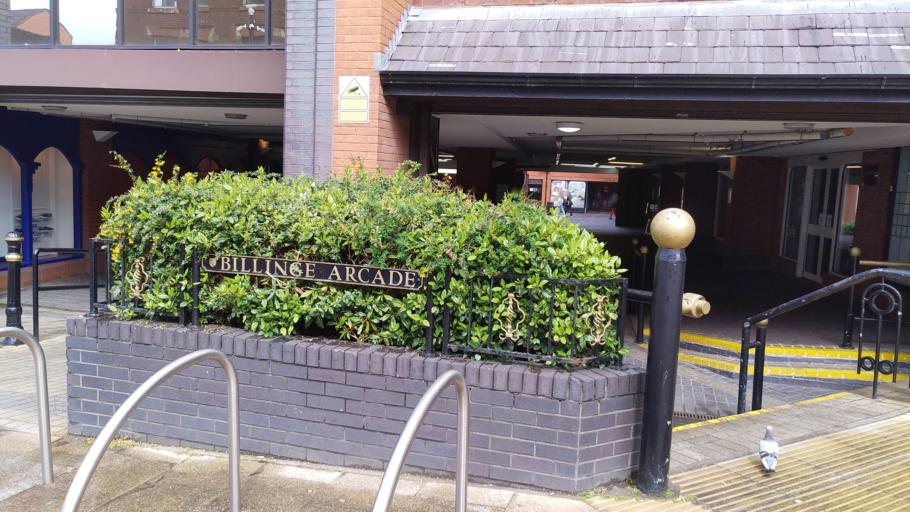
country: GB
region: England
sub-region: Borough of Wigan
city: Ince-in-Makerfield
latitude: 53.5472
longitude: -2.6327
